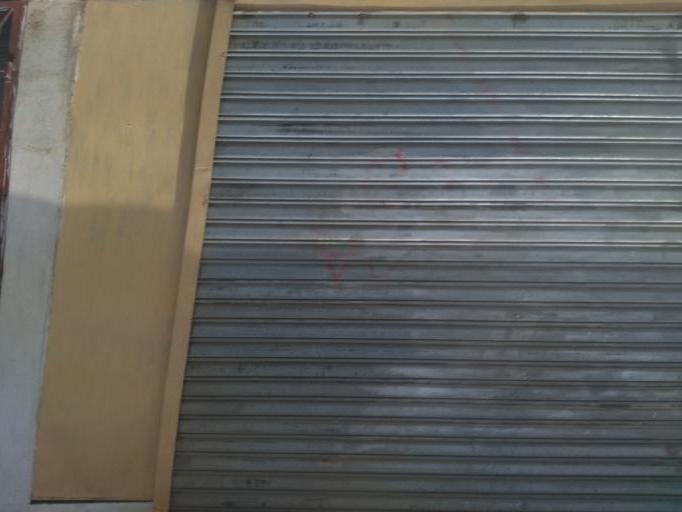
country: TZ
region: Zanzibar Urban/West
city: Zanzibar
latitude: -6.1623
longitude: 39.2065
